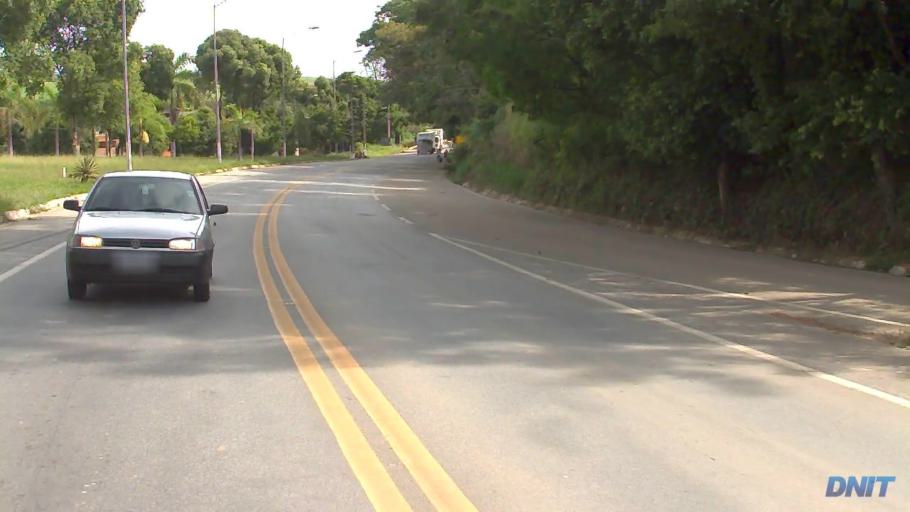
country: BR
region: Minas Gerais
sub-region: Belo Oriente
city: Belo Oriente
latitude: -19.2338
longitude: -42.3294
